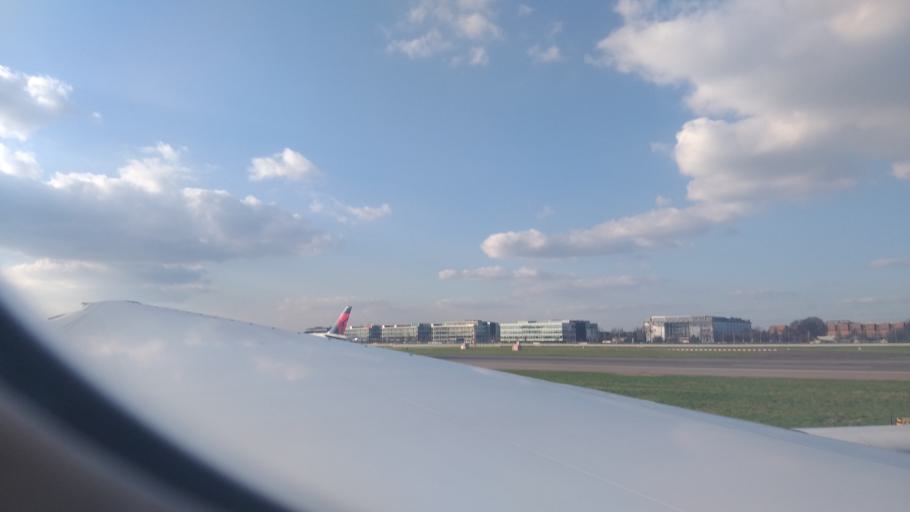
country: GB
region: England
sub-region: Greater London
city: Feltham
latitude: 51.4764
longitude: -0.4350
